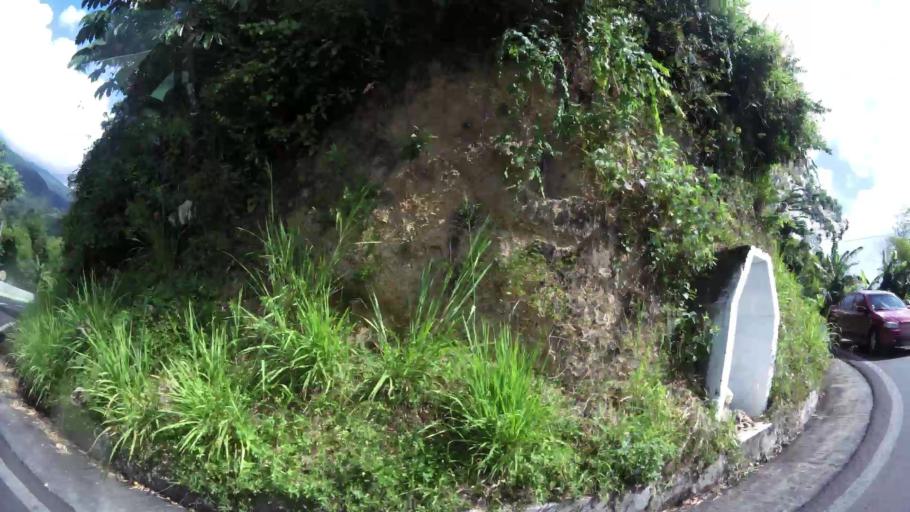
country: MQ
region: Martinique
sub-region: Martinique
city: Saint-Pierre
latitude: 14.7603
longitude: -61.1585
